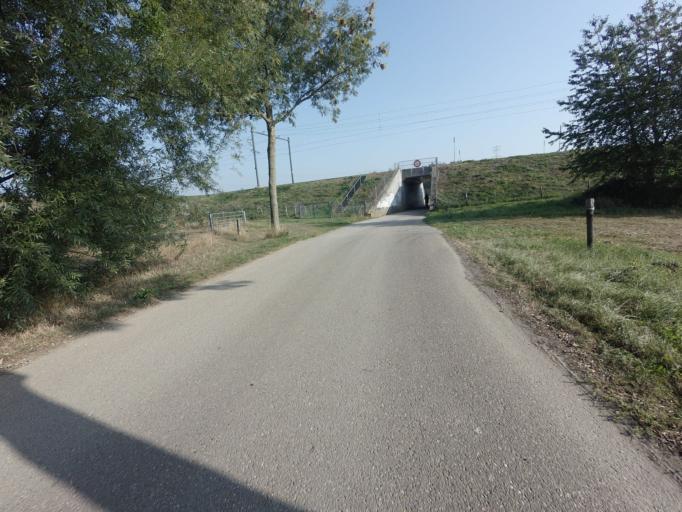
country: NL
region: Limburg
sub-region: Gemeente Roermond
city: Leeuwen
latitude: 51.2189
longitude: 5.9912
